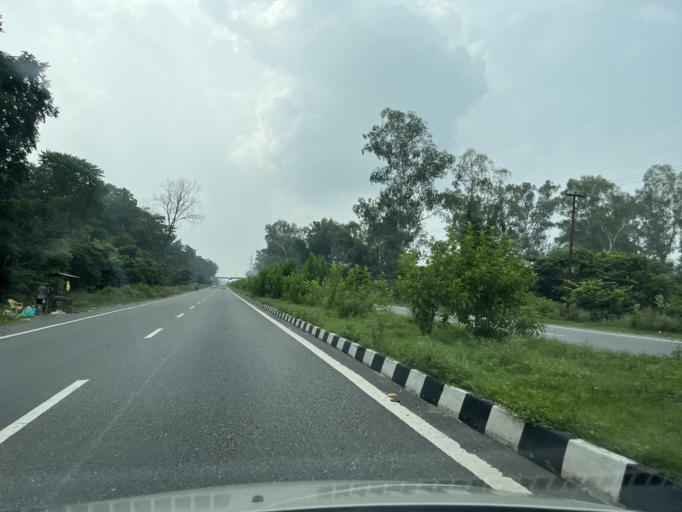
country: IN
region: Uttarakhand
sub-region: Dehradun
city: Doiwala
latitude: 30.1094
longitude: 78.1714
